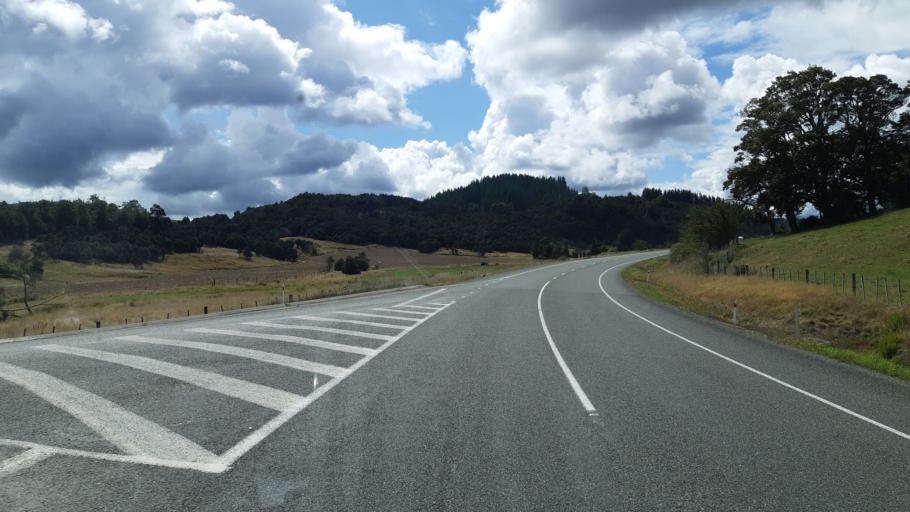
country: NZ
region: Tasman
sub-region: Tasman District
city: Wakefield
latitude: -41.6429
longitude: 172.6603
